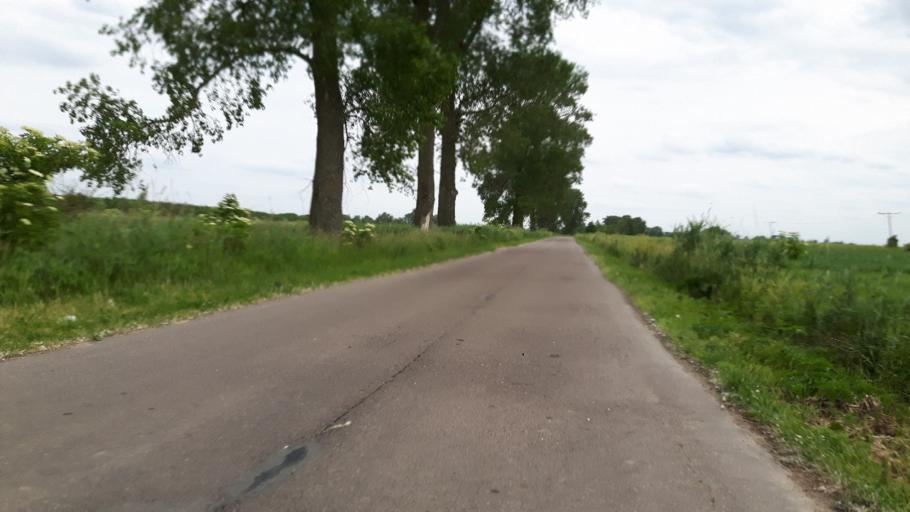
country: PL
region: Pomeranian Voivodeship
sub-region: Powiat nowodworski
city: Sztutowo
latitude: 54.2531
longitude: 19.2390
